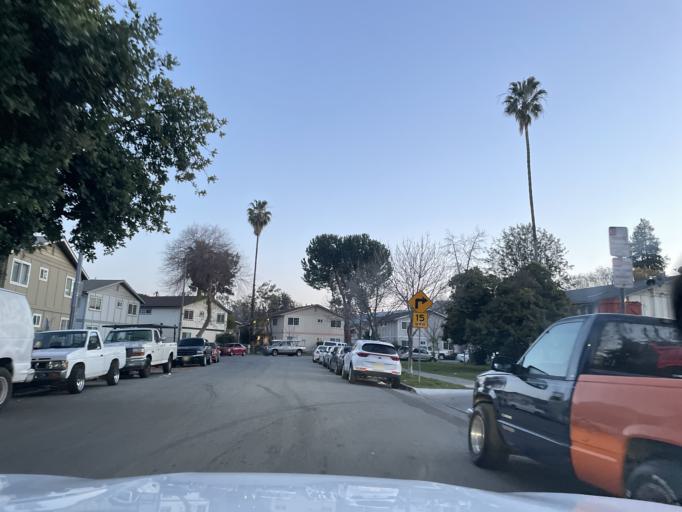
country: US
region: California
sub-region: Santa Clara County
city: Seven Trees
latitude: 37.2471
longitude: -121.8762
